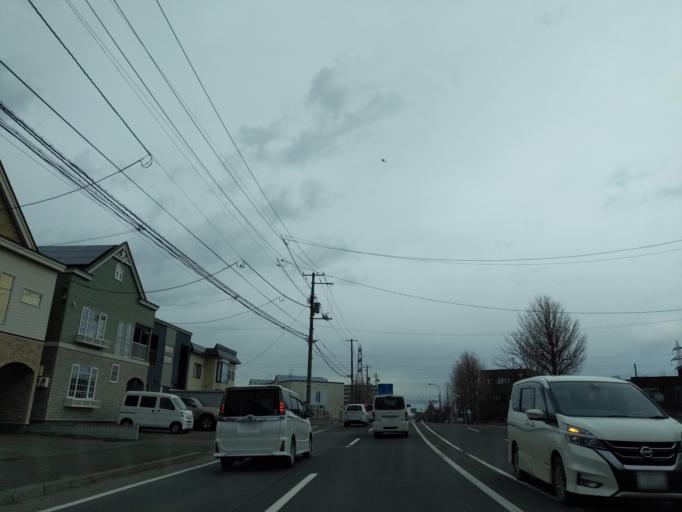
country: JP
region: Hokkaido
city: Sapporo
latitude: 43.1373
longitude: 141.3686
